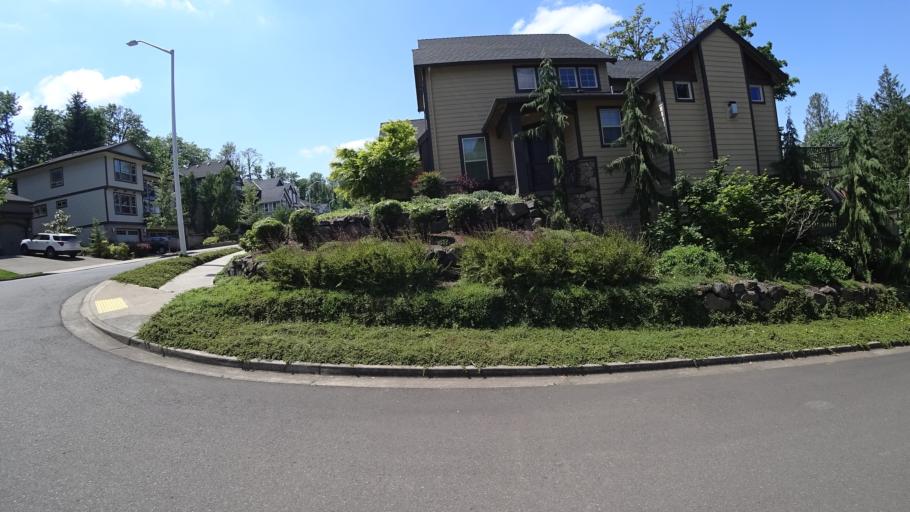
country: US
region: Oregon
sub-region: Clackamas County
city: Lake Oswego
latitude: 45.4371
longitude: -122.6912
